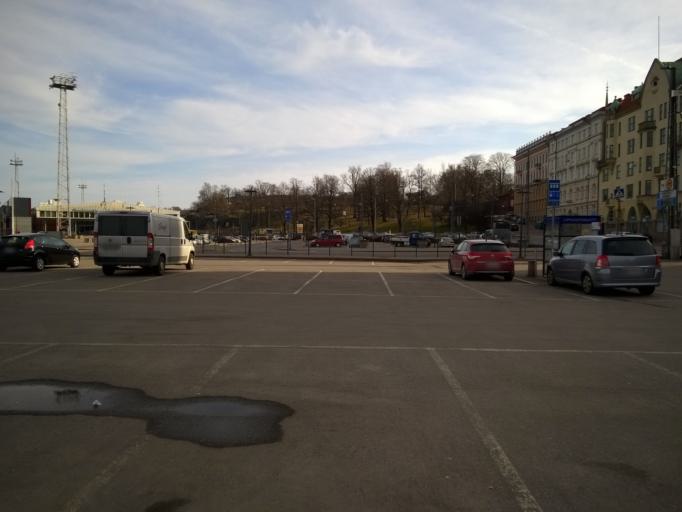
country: FI
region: Uusimaa
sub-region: Helsinki
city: Helsinki
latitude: 60.1653
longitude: 24.9533
